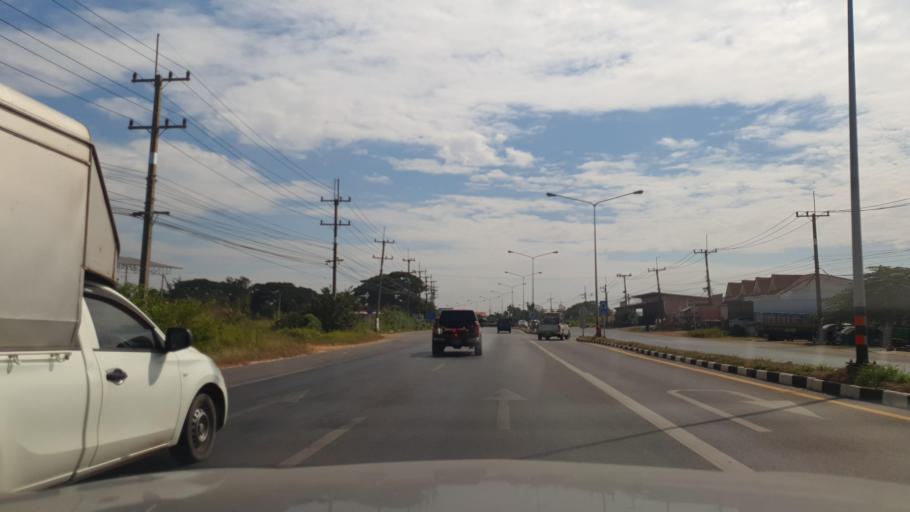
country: TH
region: Kalasin
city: Yang Talat
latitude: 16.4045
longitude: 103.4290
